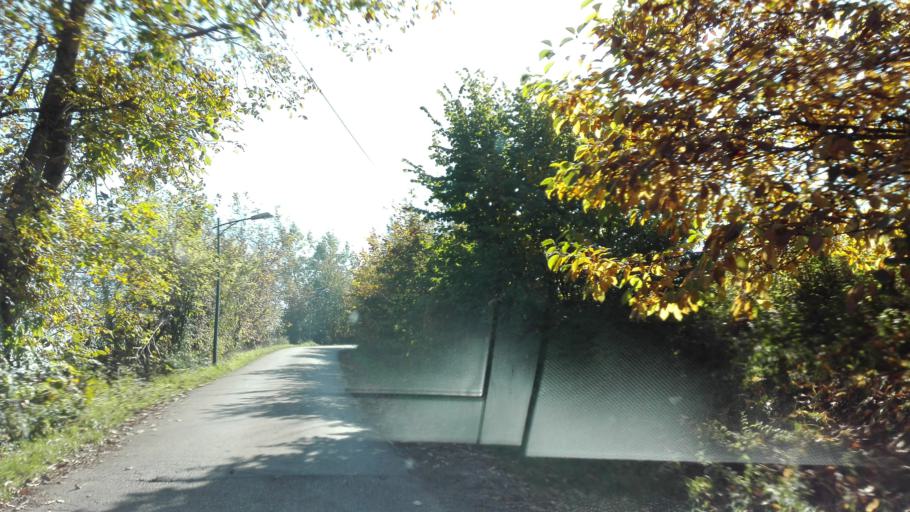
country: AT
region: Upper Austria
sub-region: Politischer Bezirk Linz-Land
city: Leonding
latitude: 48.2844
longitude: 14.2667
